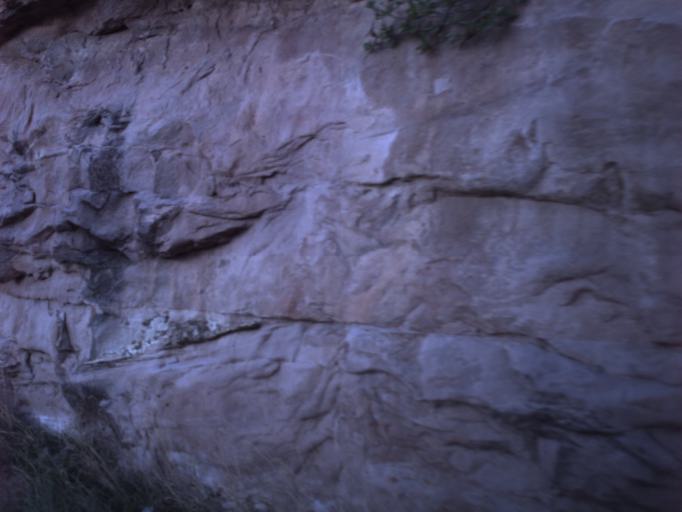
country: US
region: Utah
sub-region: Grand County
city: Moab
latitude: 38.6099
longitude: -109.5493
